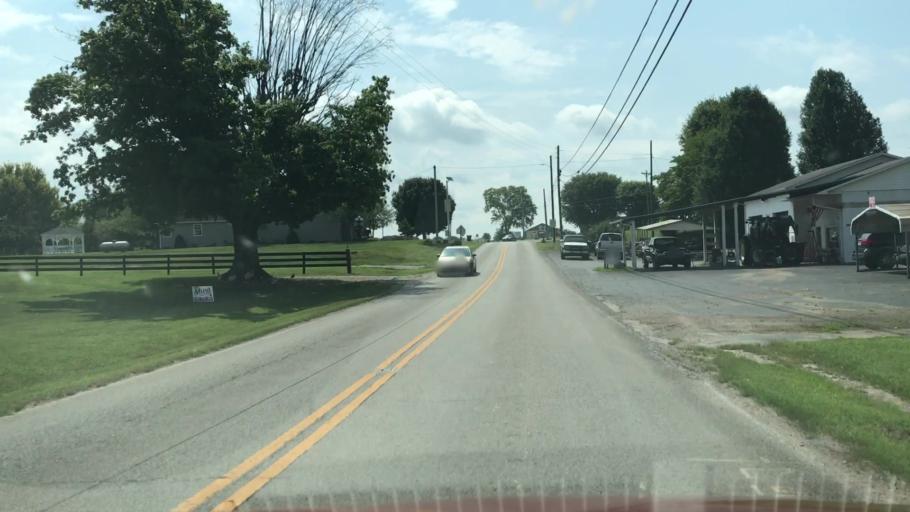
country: US
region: Kentucky
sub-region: Barren County
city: Glasgow
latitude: 36.8857
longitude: -85.8464
